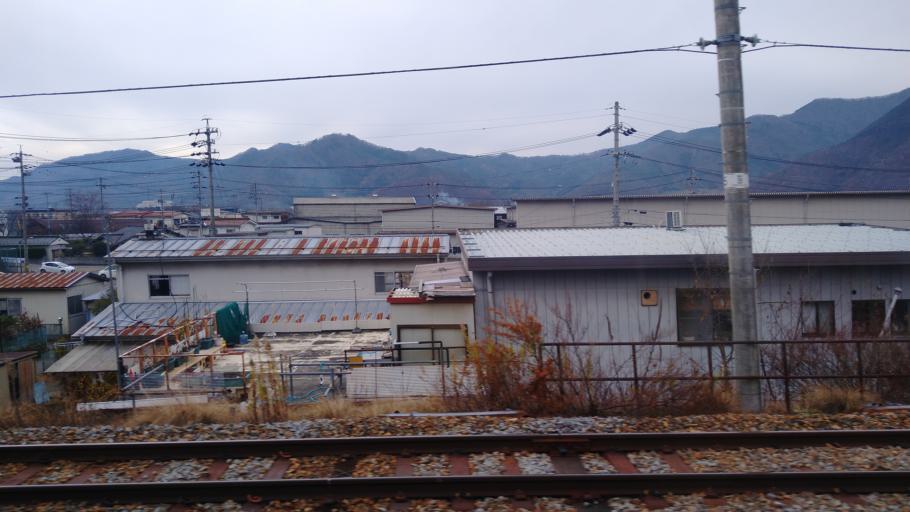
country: JP
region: Nagano
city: Ueda
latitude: 36.4648
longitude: 138.1773
